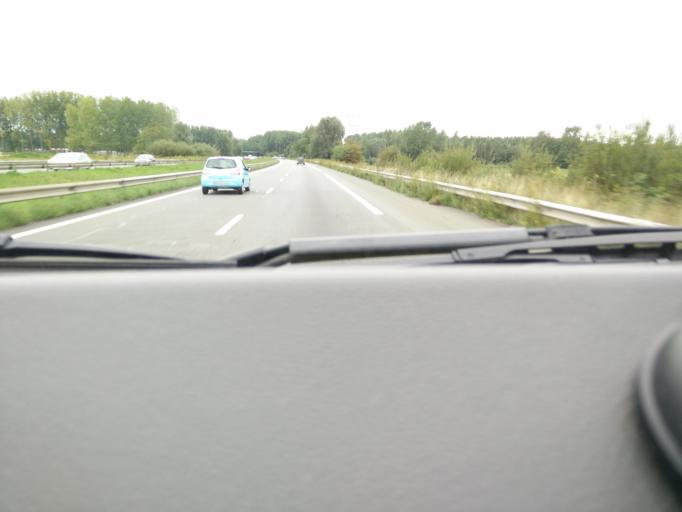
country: FR
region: Nord-Pas-de-Calais
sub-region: Departement du Nord
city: Genech
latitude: 50.5411
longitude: 3.1960
